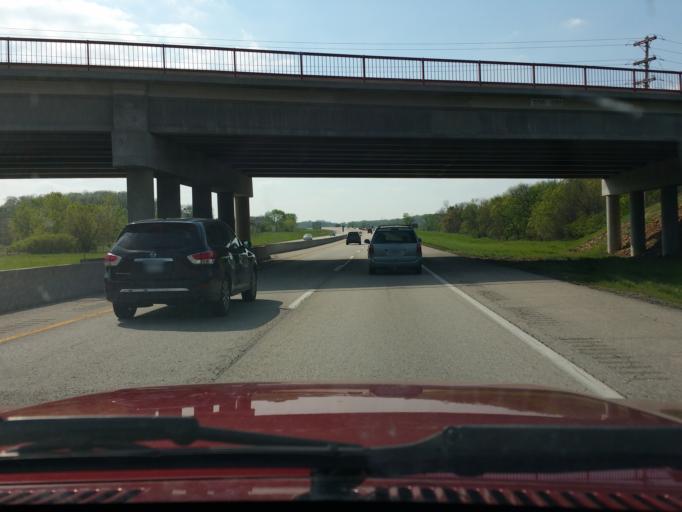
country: US
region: Kansas
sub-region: Douglas County
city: Lawrence
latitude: 38.9953
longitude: -95.2787
